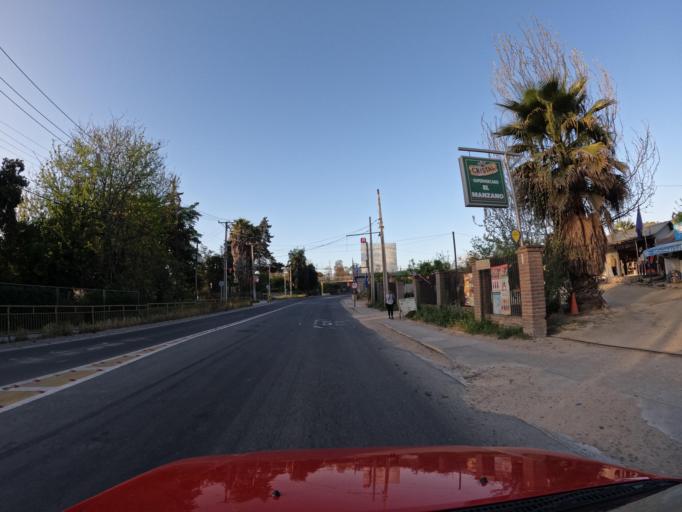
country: CL
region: O'Higgins
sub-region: Provincia de Cachapoal
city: San Vicente
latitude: -34.1802
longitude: -71.4000
